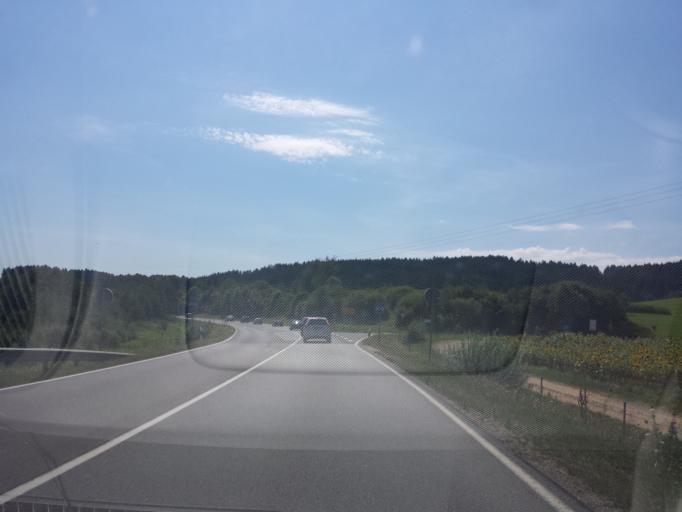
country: DE
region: Bavaria
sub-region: Upper Palatinate
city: Traitsching
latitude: 49.1478
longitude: 12.6480
